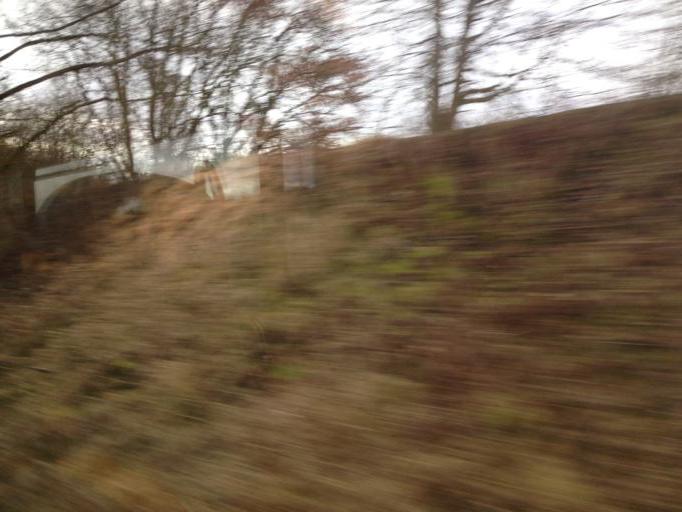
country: DE
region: Hesse
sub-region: Regierungsbezirk Giessen
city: Lich
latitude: 50.5276
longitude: 8.7541
